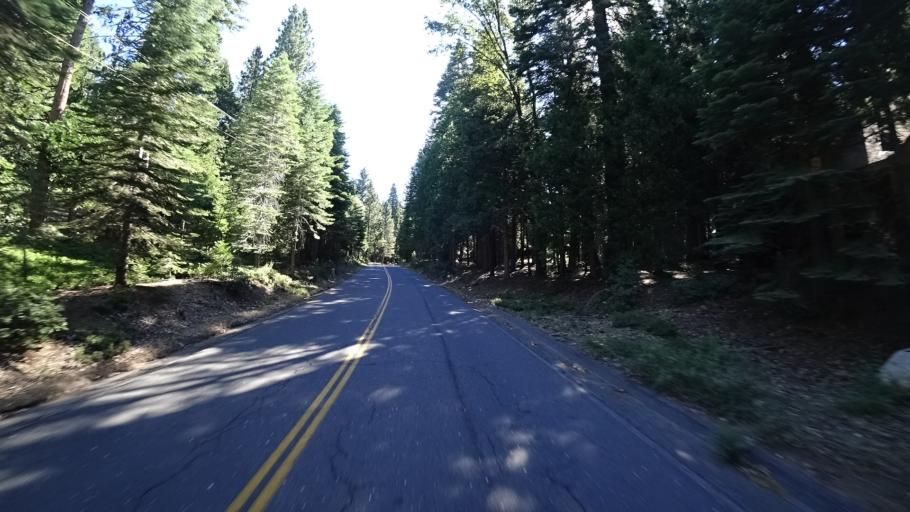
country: US
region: California
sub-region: Calaveras County
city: Arnold
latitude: 38.2994
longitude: -120.2706
